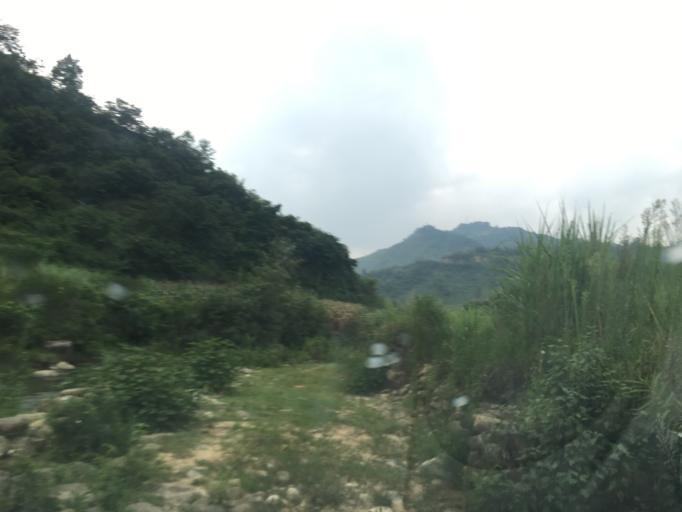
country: CN
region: Guangxi Zhuangzu Zizhiqu
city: Xinzhou
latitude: 25.1709
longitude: 105.6988
